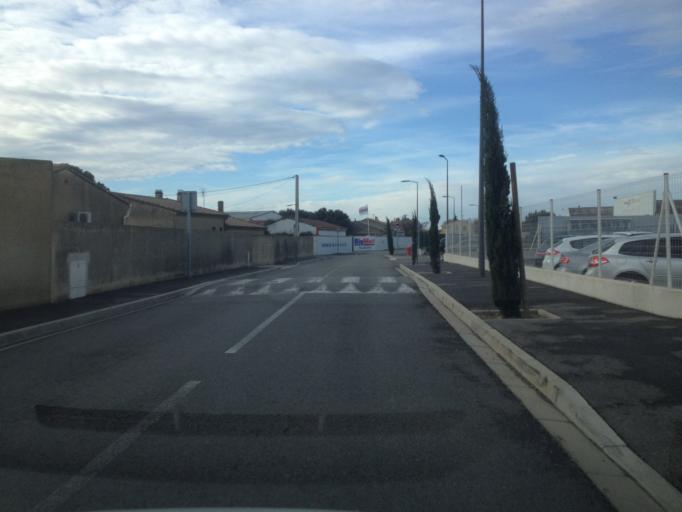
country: FR
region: Provence-Alpes-Cote d'Azur
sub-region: Departement du Vaucluse
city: Sorgues
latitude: 44.0142
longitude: 4.8839
